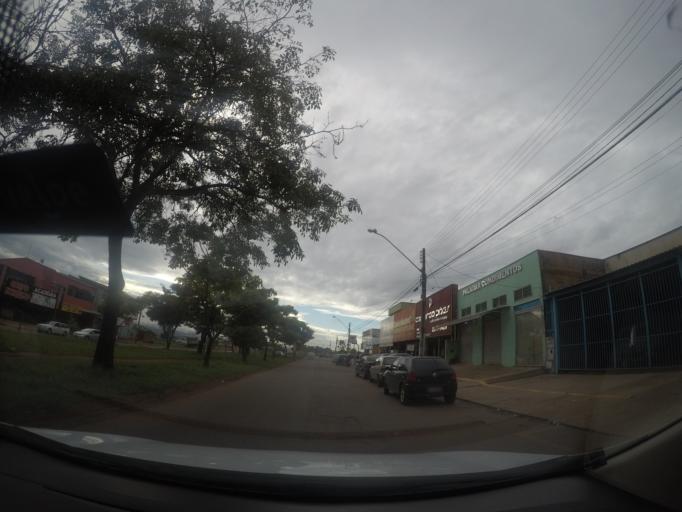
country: BR
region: Goias
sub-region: Goiania
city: Goiania
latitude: -16.6061
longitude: -49.3107
